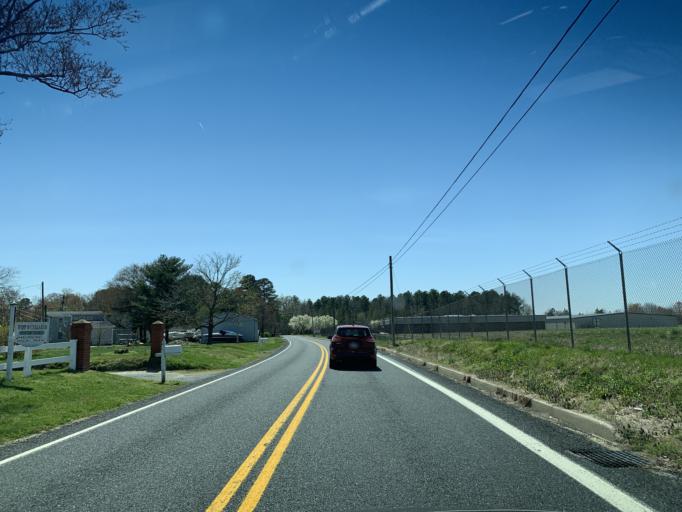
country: US
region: Maryland
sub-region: Talbot County
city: Easton
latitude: 38.8048
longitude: -76.0619
